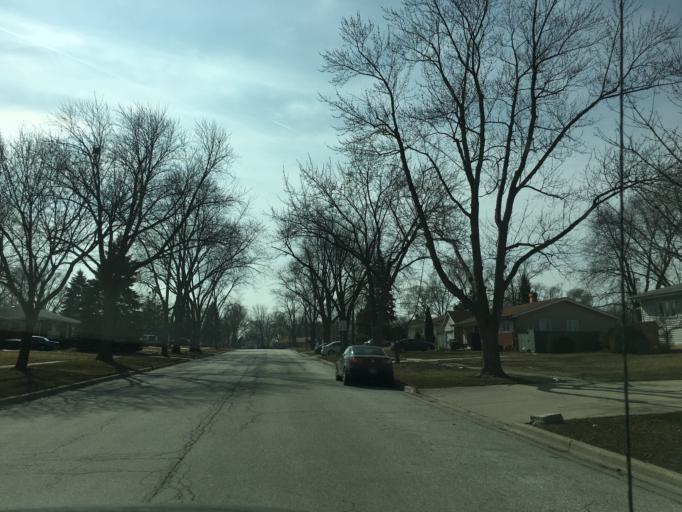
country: US
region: Illinois
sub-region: Cook County
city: Schaumburg
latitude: 42.0340
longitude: -88.0960
